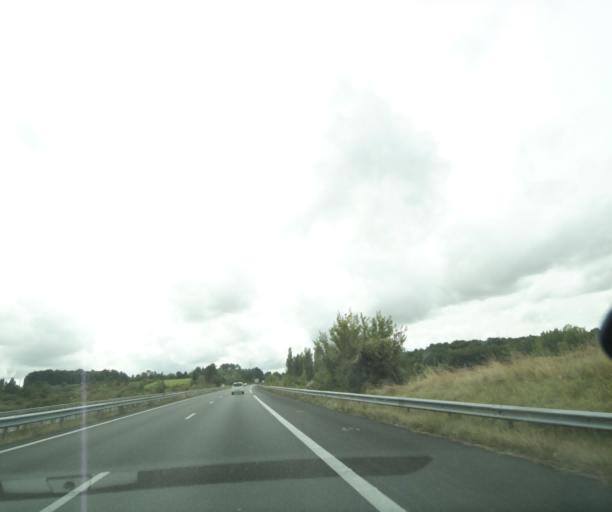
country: FR
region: Poitou-Charentes
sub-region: Departement de la Charente-Maritime
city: Mirambeau
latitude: 45.4110
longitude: -0.6016
